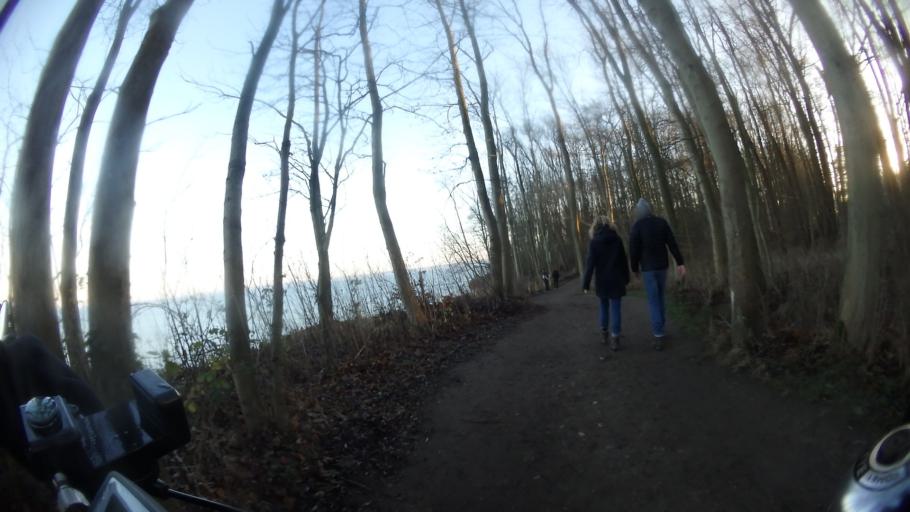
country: DE
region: Schleswig-Holstein
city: Travemuende
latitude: 53.9866
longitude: 10.8765
